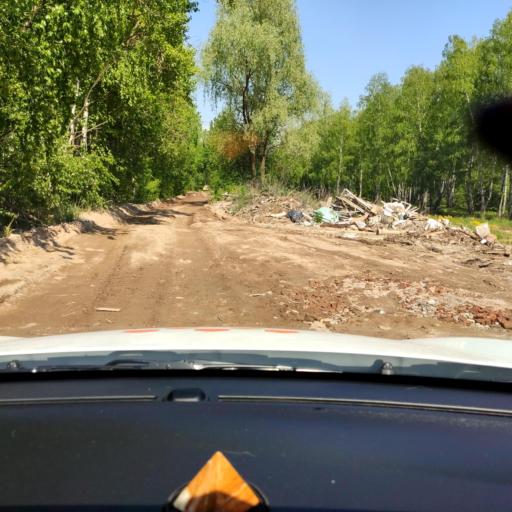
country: RU
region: Tatarstan
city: Stolbishchi
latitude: 55.7058
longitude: 49.1836
